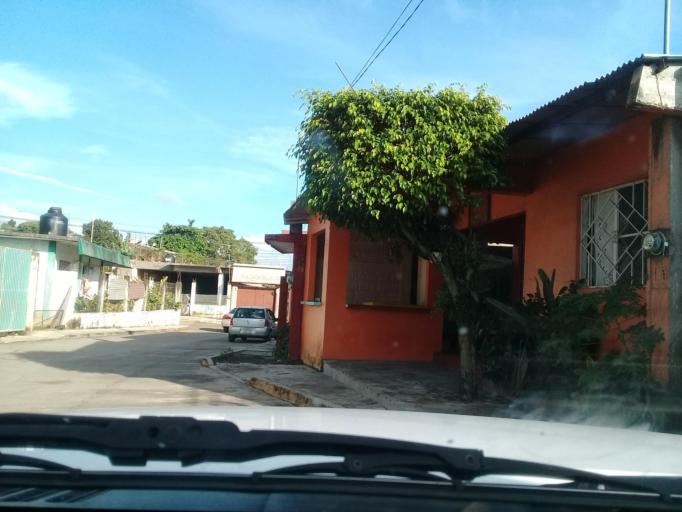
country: MX
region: Veracruz
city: Catemaco
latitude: 18.4277
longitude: -95.1096
